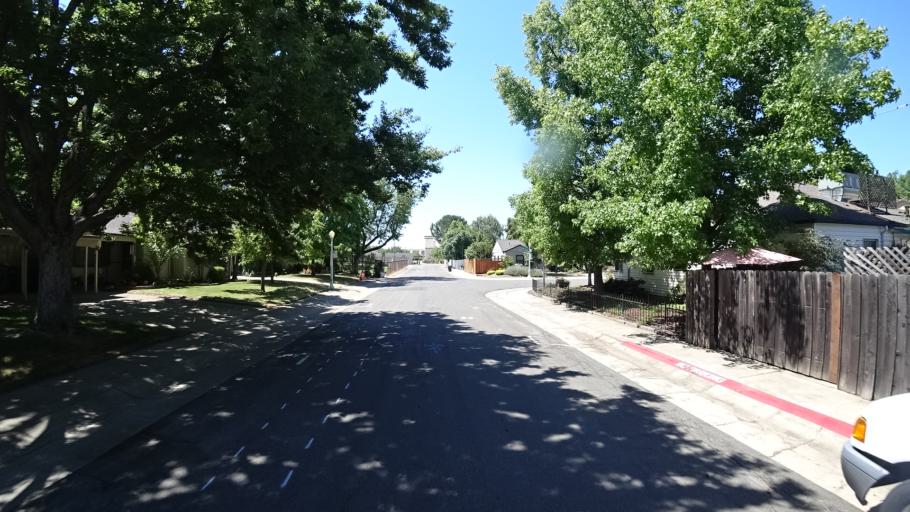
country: US
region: California
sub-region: Sacramento County
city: Sacramento
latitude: 38.5434
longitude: -121.4879
